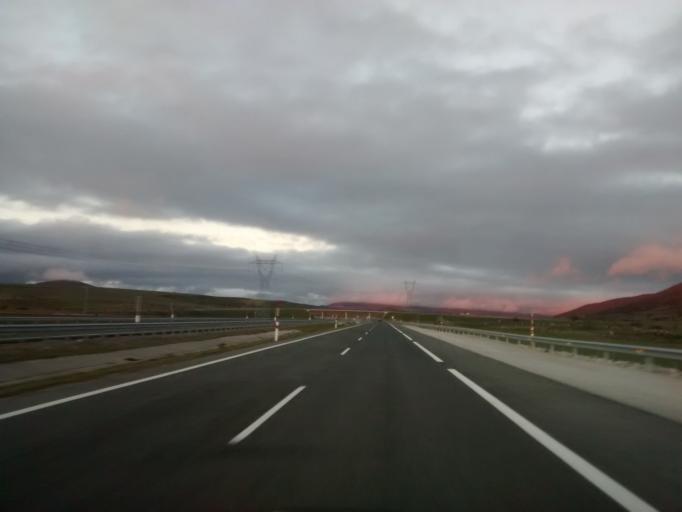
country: ES
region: Cantabria
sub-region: Provincia de Cantabria
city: Mataporquera
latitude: 42.8465
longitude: -4.1724
